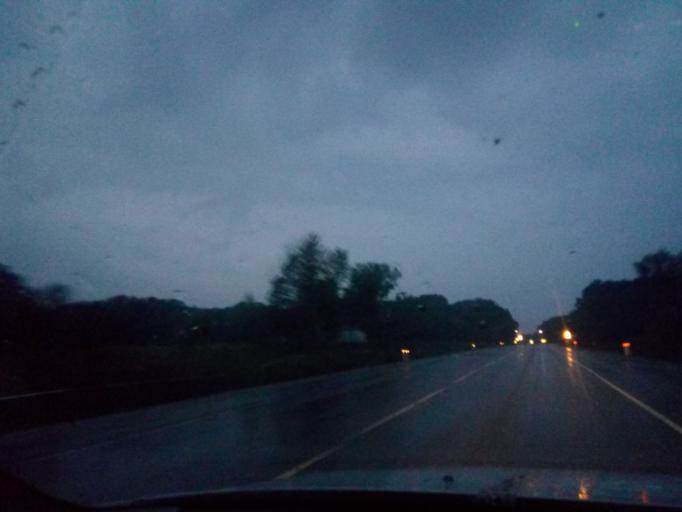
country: RU
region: Primorskiy
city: Dal'nerechensk
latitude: 45.8879
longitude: 133.7324
